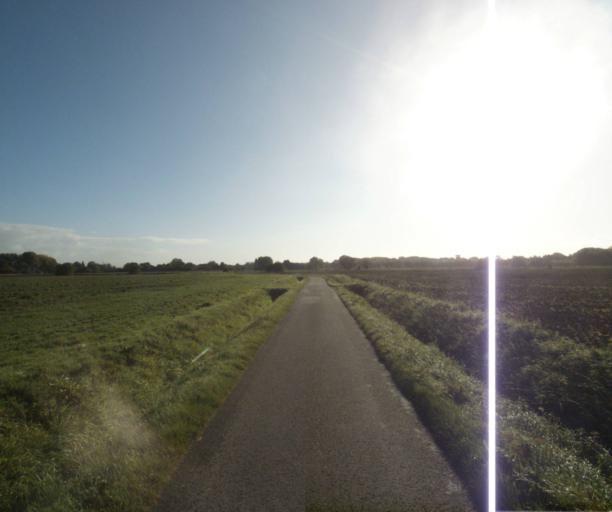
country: FR
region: Nord-Pas-de-Calais
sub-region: Departement du Nord
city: Verlinghem
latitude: 50.6665
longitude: 3.0151
